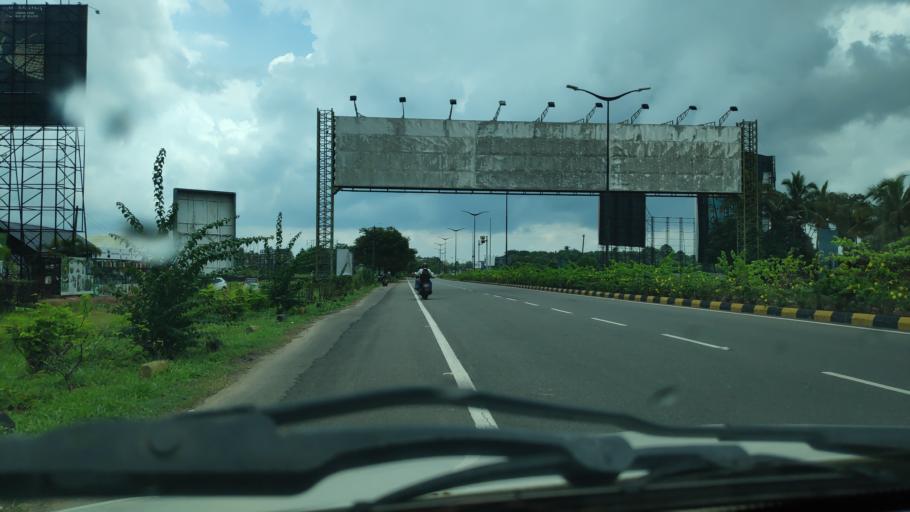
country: IN
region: Kerala
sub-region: Ernakulam
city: Aluva
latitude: 10.1503
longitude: 76.3627
